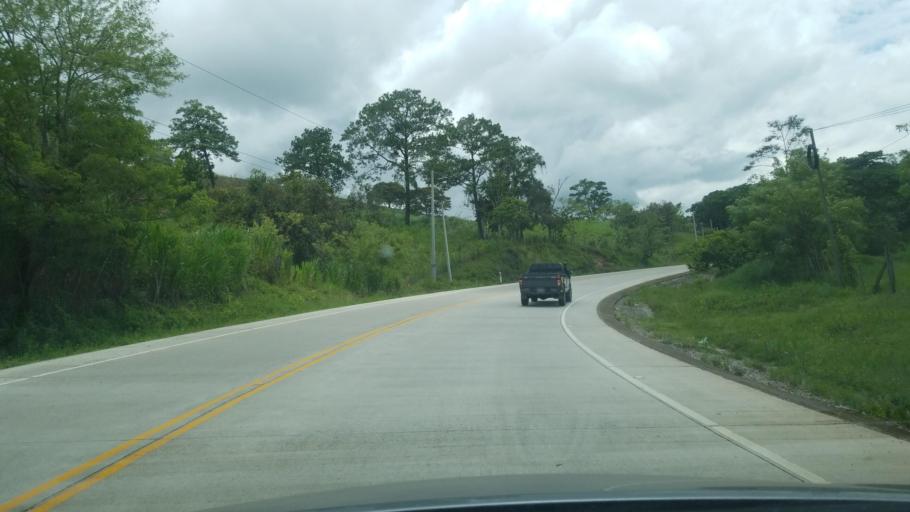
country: HN
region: Copan
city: San Jeronimo
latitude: 14.9850
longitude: -88.8636
